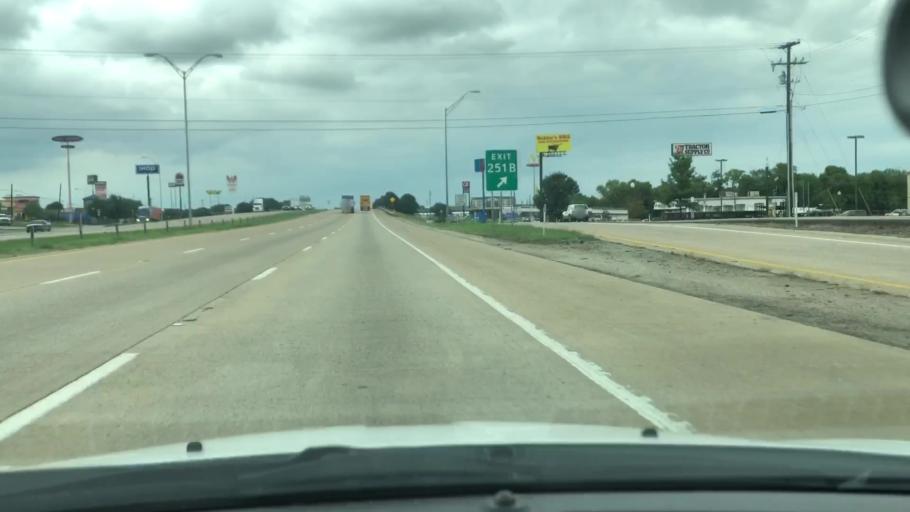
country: US
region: Texas
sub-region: Ellis County
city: Ennis
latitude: 32.3313
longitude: -96.6134
